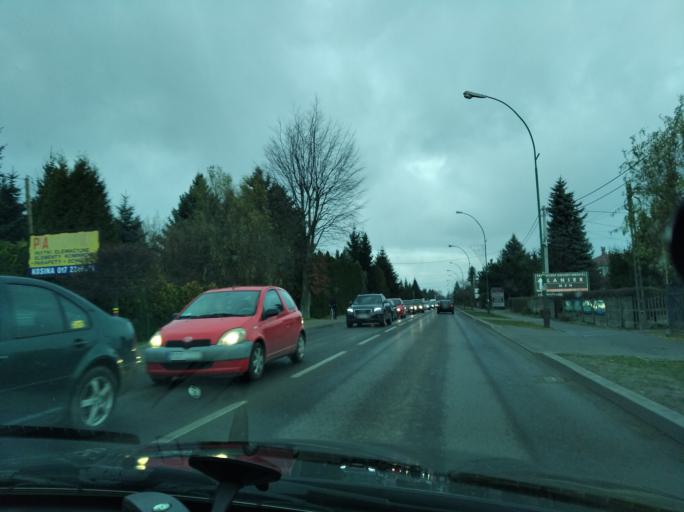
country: PL
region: Subcarpathian Voivodeship
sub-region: Powiat lancucki
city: Lancut
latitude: 50.0844
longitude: 22.2325
